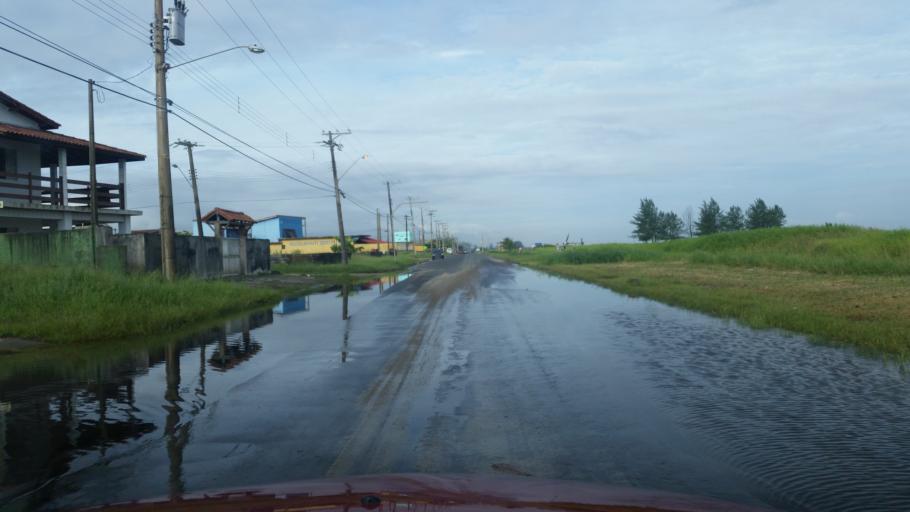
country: BR
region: Sao Paulo
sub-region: Iguape
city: Iguape
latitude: -24.7630
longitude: -47.5740
